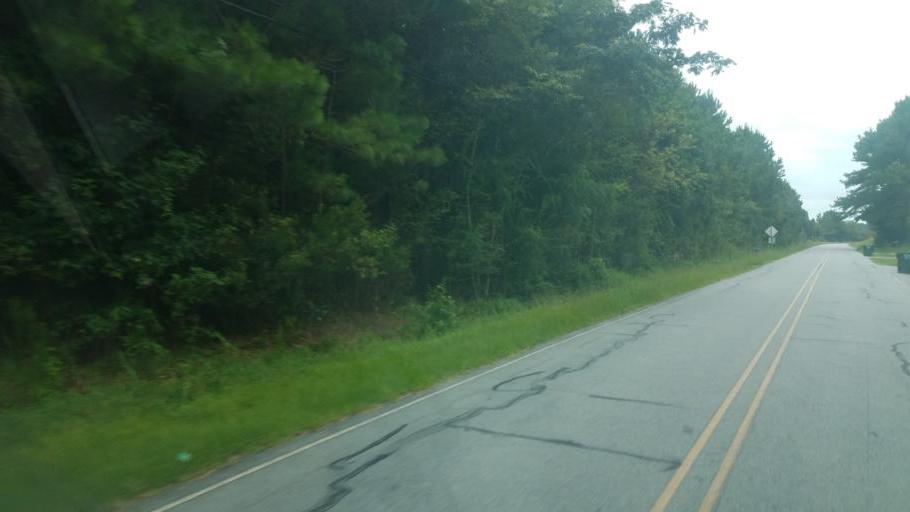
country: US
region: North Carolina
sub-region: Tyrrell County
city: Columbia
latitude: 35.9096
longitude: -76.2919
